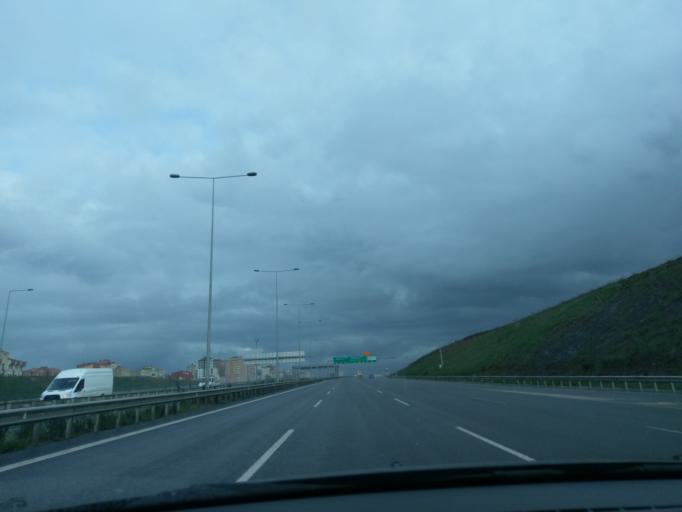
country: TR
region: Istanbul
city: Basaksehir
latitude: 41.0940
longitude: 28.8135
